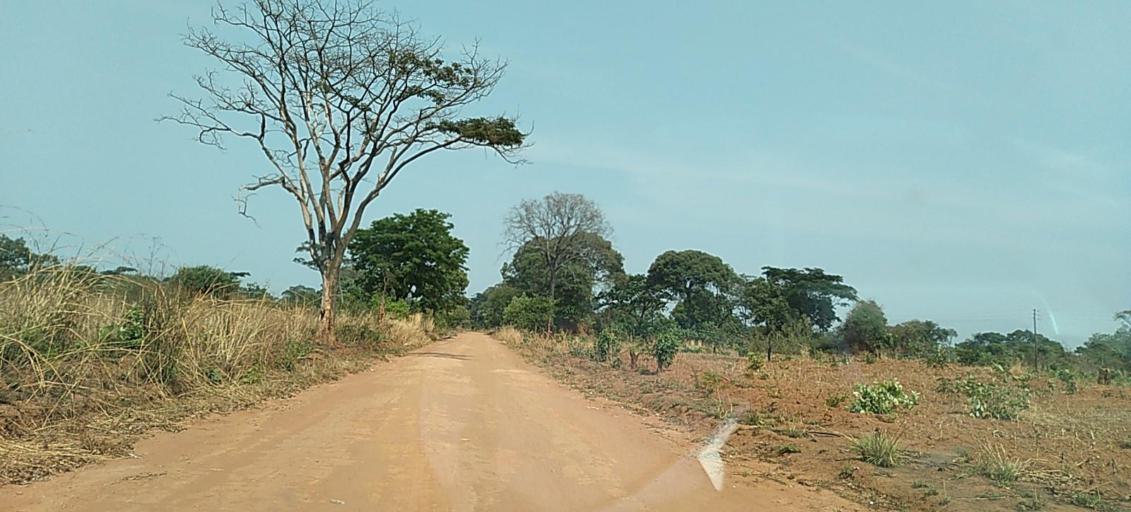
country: ZM
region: Copperbelt
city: Chililabombwe
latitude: -12.3409
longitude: 27.6955
